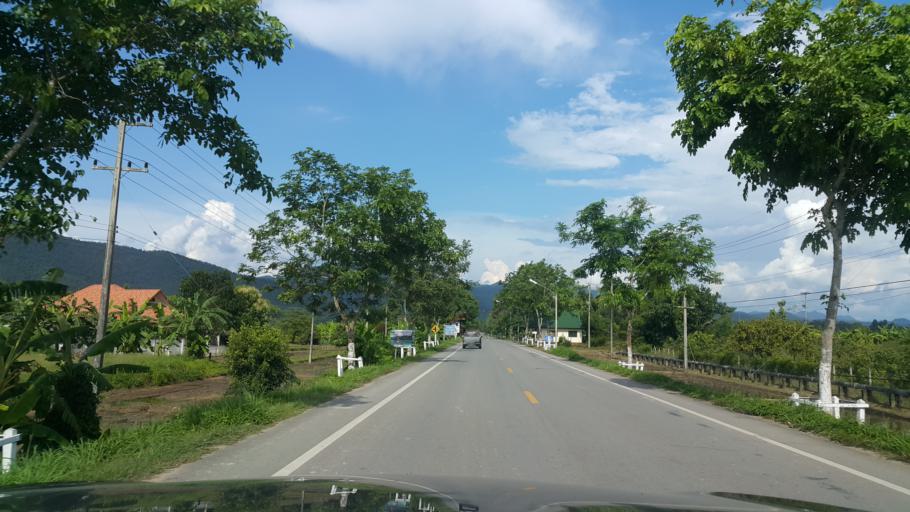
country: TH
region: Chiang Mai
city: Mae Taeng
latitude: 19.1438
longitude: 99.0244
